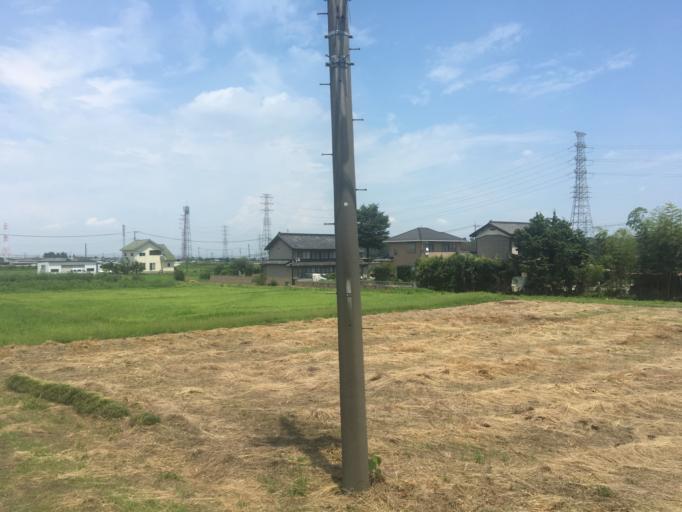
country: JP
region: Saitama
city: Kodamacho-kodamaminami
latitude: 36.1720
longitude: 139.1835
